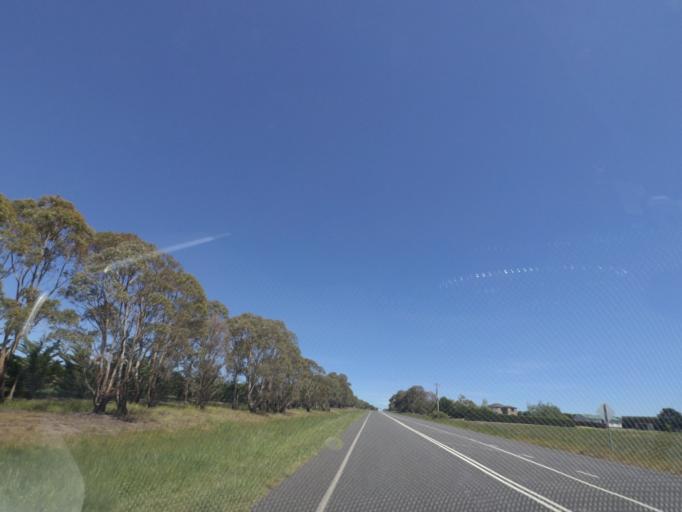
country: AU
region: Victoria
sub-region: Hume
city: Sunbury
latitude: -37.5416
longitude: 144.6378
